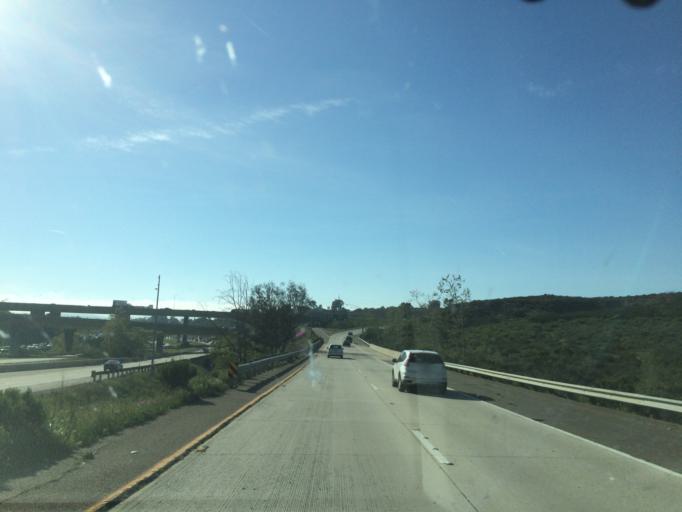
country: US
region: California
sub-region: San Diego County
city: La Jolla
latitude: 32.8471
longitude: -117.1727
